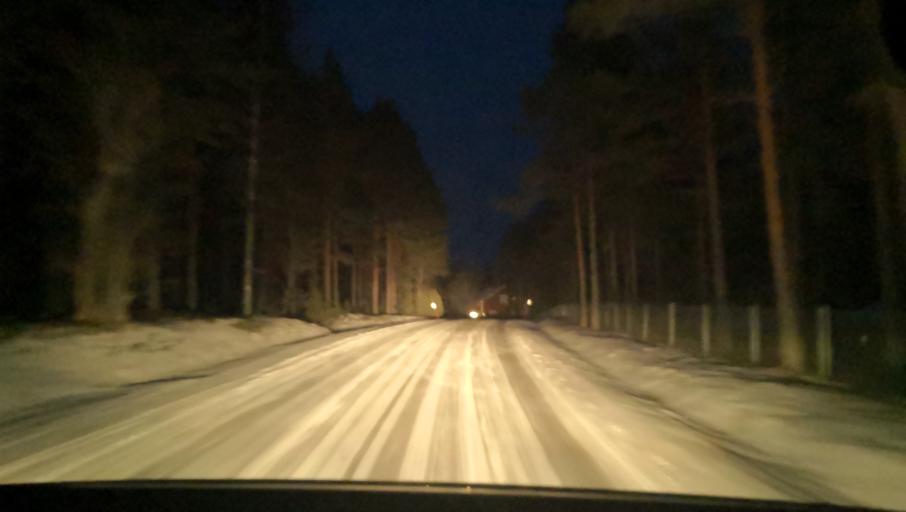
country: SE
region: Uppsala
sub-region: Heby Kommun
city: Tarnsjo
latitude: 60.2842
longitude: 16.8054
